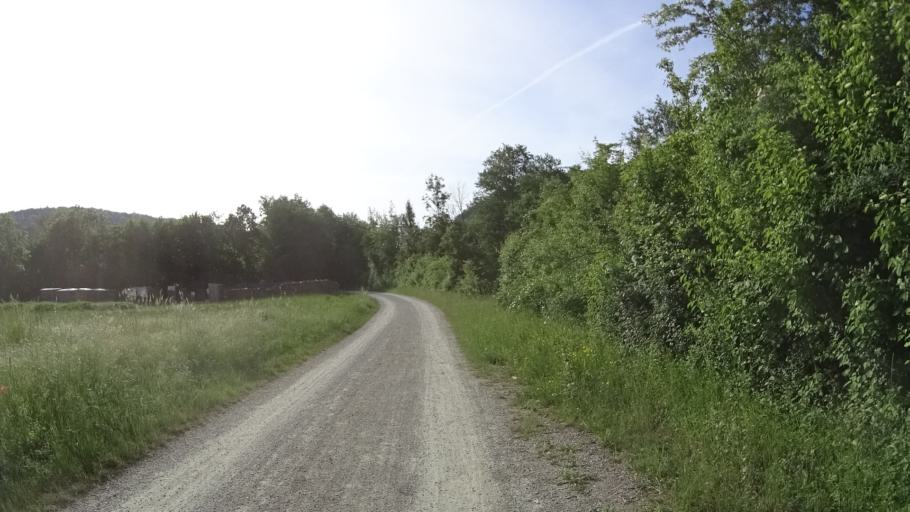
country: DE
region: Bavaria
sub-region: Lower Bavaria
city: Riedenburg
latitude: 48.9543
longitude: 11.7207
